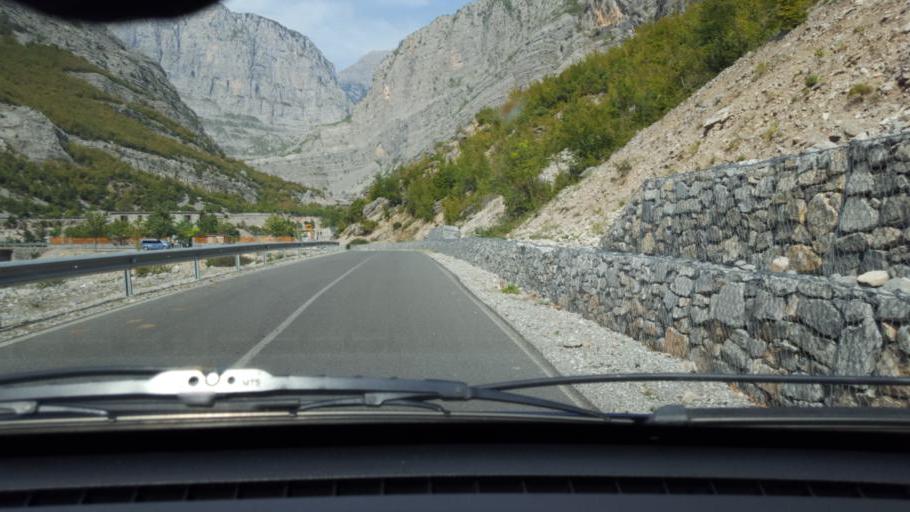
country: AL
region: Shkoder
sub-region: Rrethi i Malesia e Madhe
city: Kastrat
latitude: 42.4797
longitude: 19.5829
